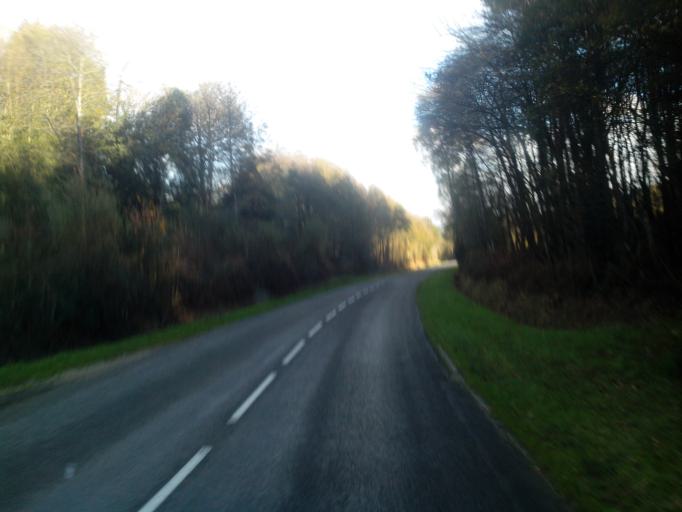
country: FR
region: Brittany
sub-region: Departement du Morbihan
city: Guilliers
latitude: 48.0247
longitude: -2.4527
